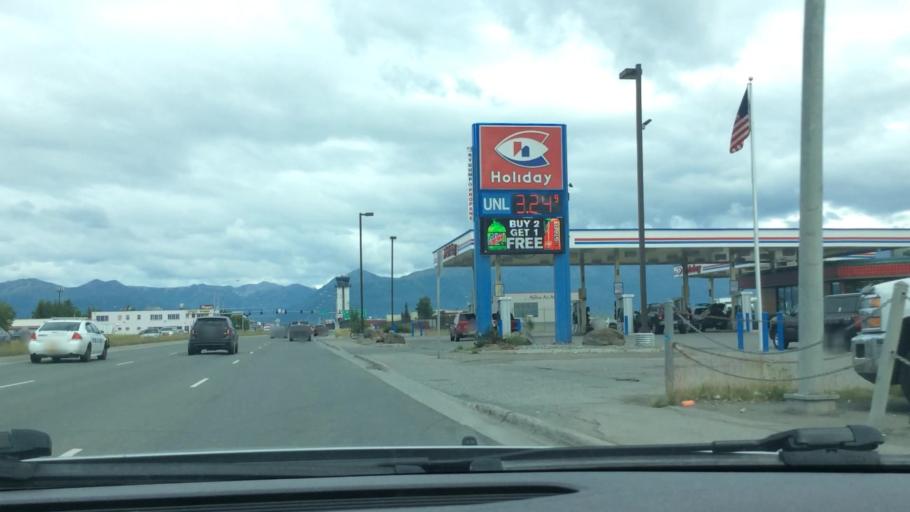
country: US
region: Alaska
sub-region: Anchorage Municipality
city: Anchorage
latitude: 61.2175
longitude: -149.8550
